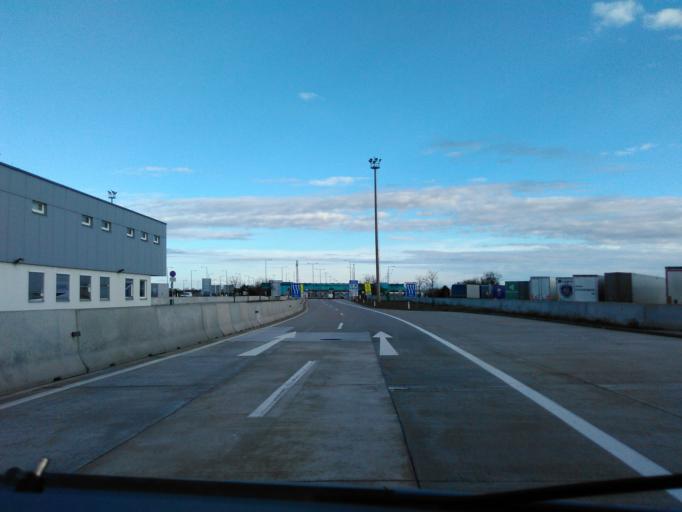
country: AT
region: Burgenland
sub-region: Politischer Bezirk Neusiedl am See
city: Kittsee
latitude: 48.0715
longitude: 17.0702
